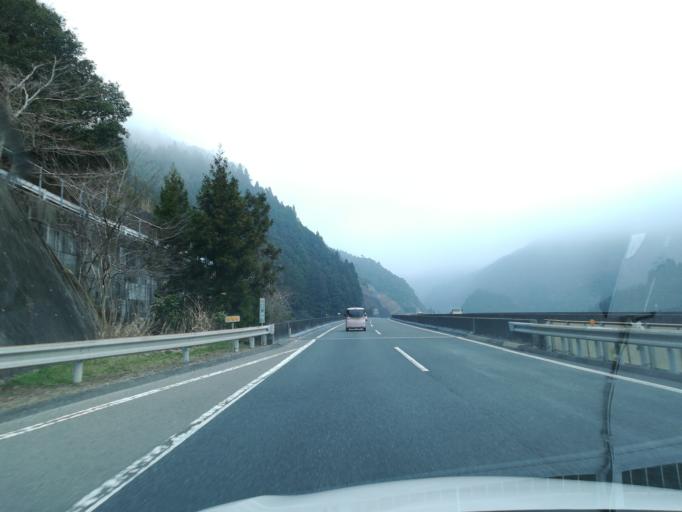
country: JP
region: Ehime
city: Kawanoecho
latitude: 33.7821
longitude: 133.6615
